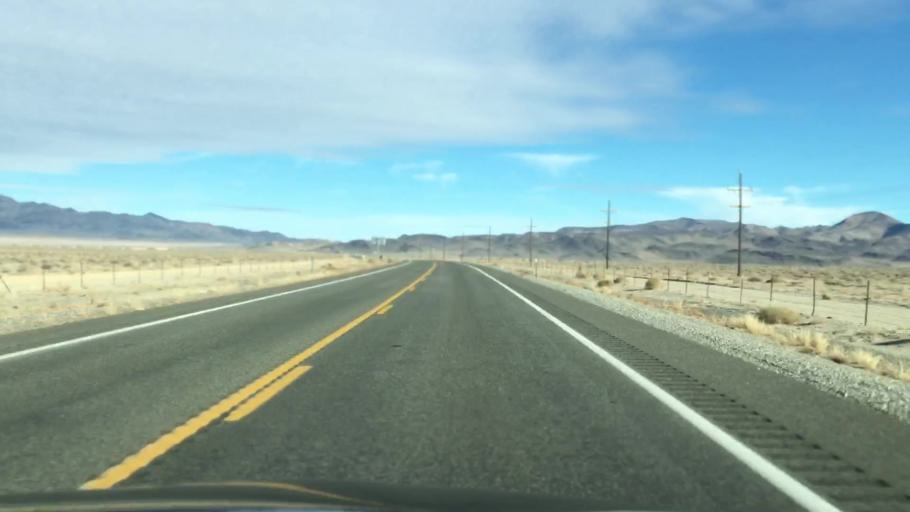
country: US
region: Nevada
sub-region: Mineral County
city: Hawthorne
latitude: 38.5248
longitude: -118.5781
